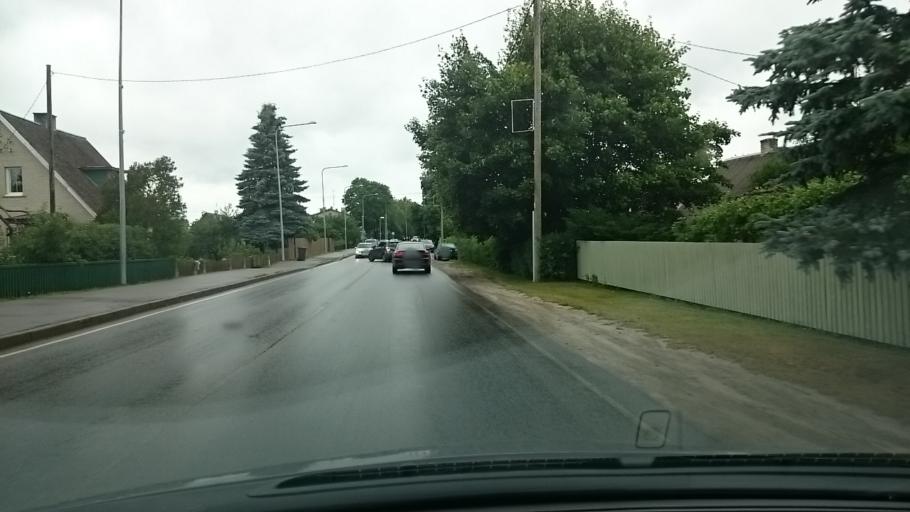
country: EE
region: Harju
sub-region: Keila linn
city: Keila
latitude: 59.3076
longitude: 24.4074
